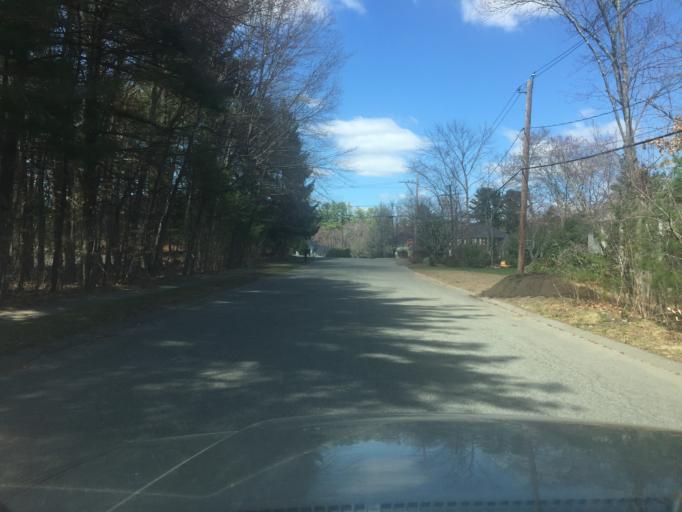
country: US
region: Massachusetts
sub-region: Norfolk County
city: Medway
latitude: 42.1735
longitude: -71.4031
